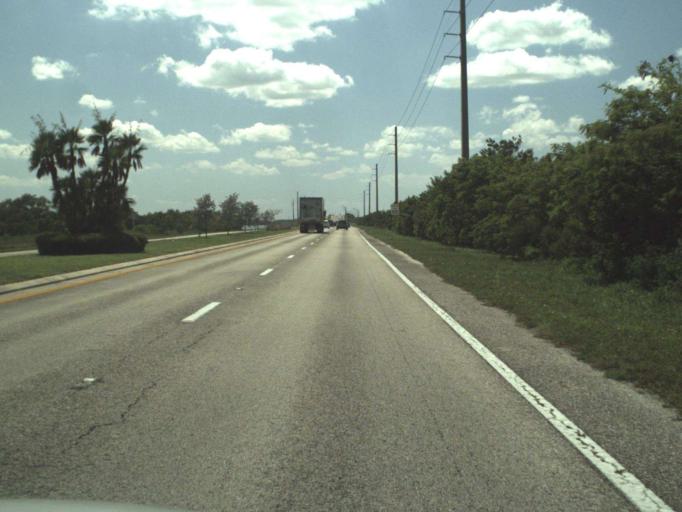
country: US
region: Florida
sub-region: Brevard County
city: Cocoa Beach
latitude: 28.3578
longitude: -80.6343
